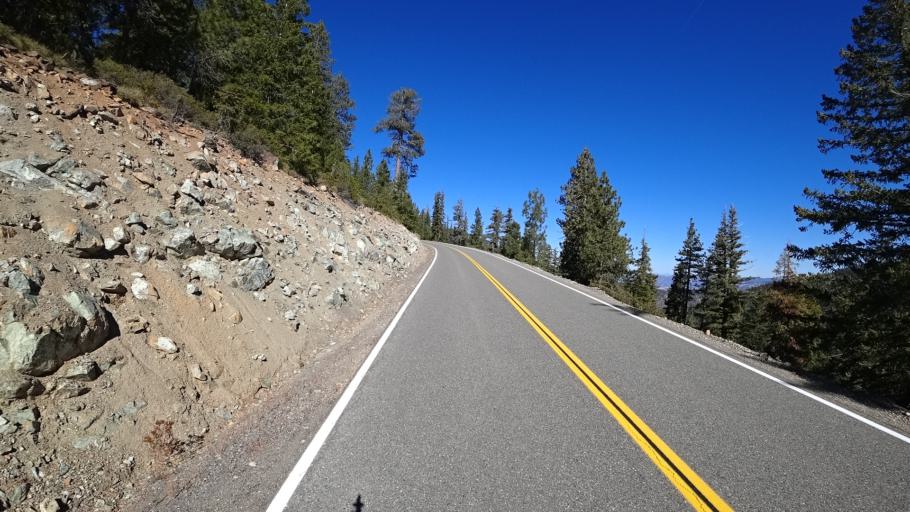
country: US
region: California
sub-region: Trinity County
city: Weaverville
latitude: 41.2374
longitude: -122.8928
